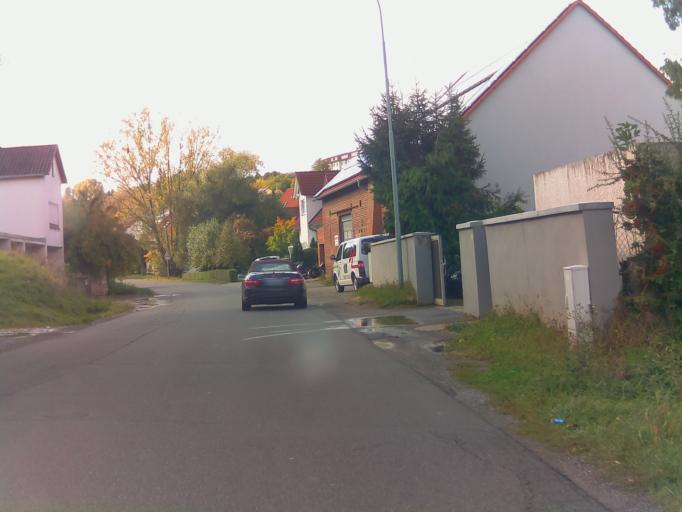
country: DE
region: Bavaria
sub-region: Regierungsbezirk Unterfranken
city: Kitzingen
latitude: 49.7382
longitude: 10.1422
